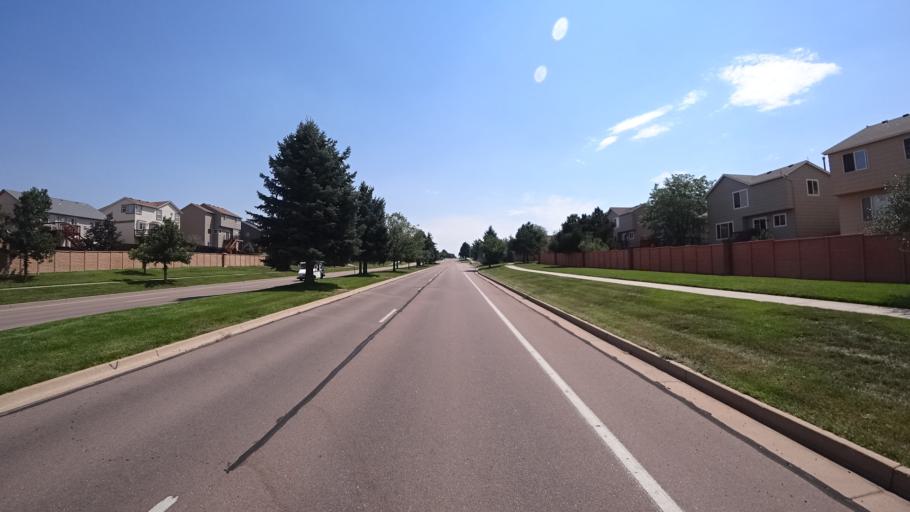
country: US
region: Colorado
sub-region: El Paso County
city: Cimarron Hills
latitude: 38.9289
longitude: -104.7336
